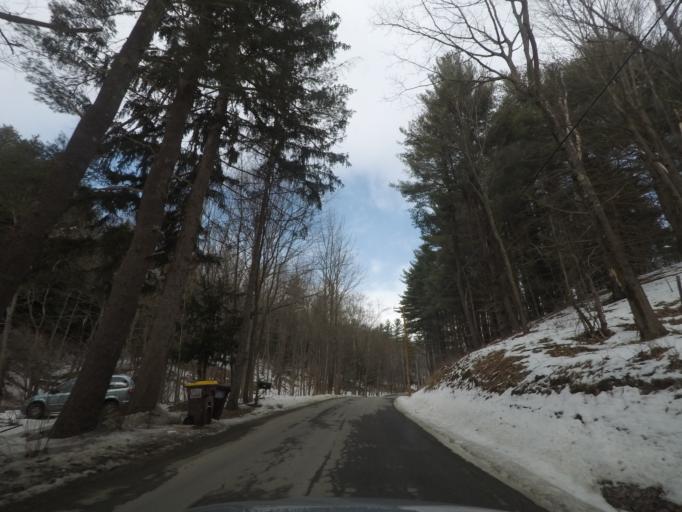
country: US
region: New York
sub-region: Saratoga County
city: Waterford
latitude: 42.7705
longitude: -73.6094
